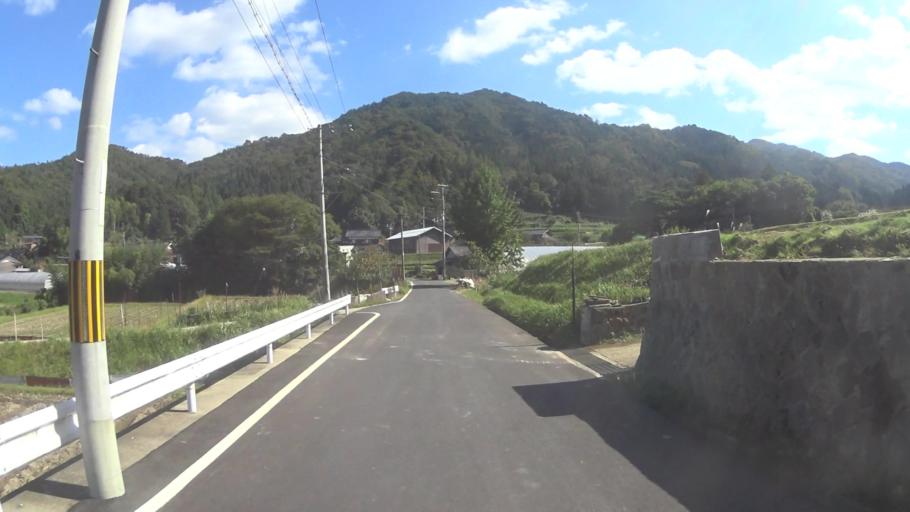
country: JP
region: Hyogo
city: Toyooka
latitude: 35.5446
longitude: 134.9769
